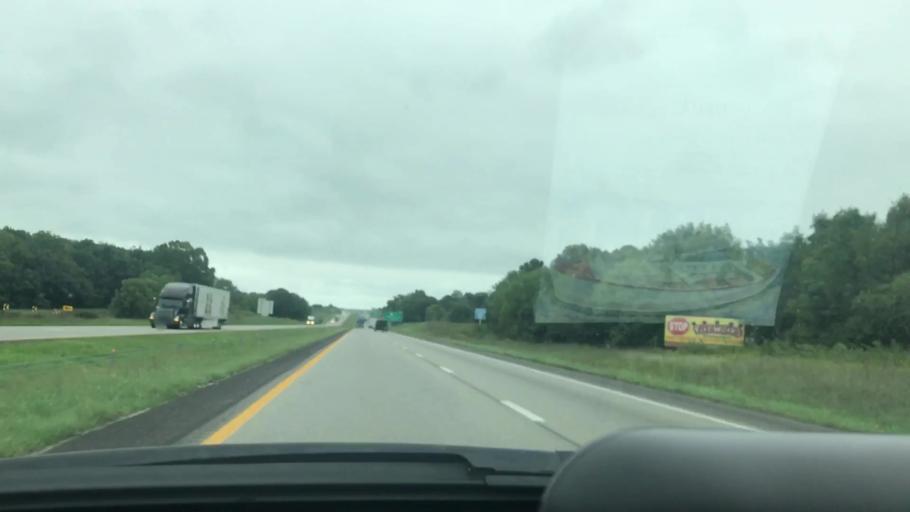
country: US
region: Missouri
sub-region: Greene County
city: Republic
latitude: 37.1924
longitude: -93.4616
